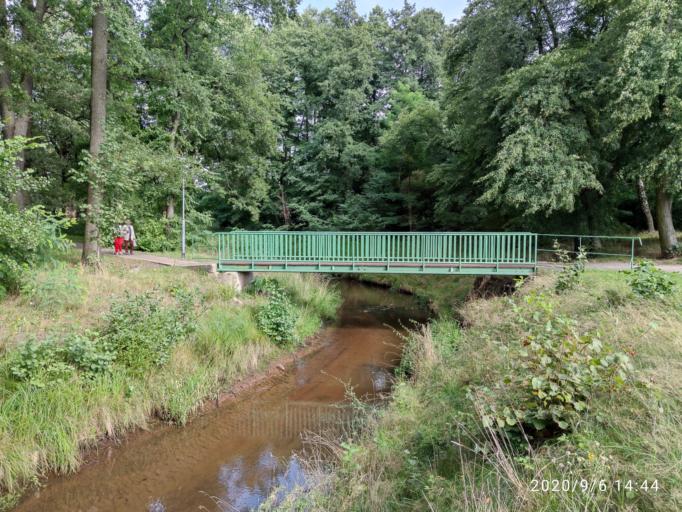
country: PL
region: Lubusz
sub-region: Powiat zarski
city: Jasien
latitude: 51.7505
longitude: 15.0227
